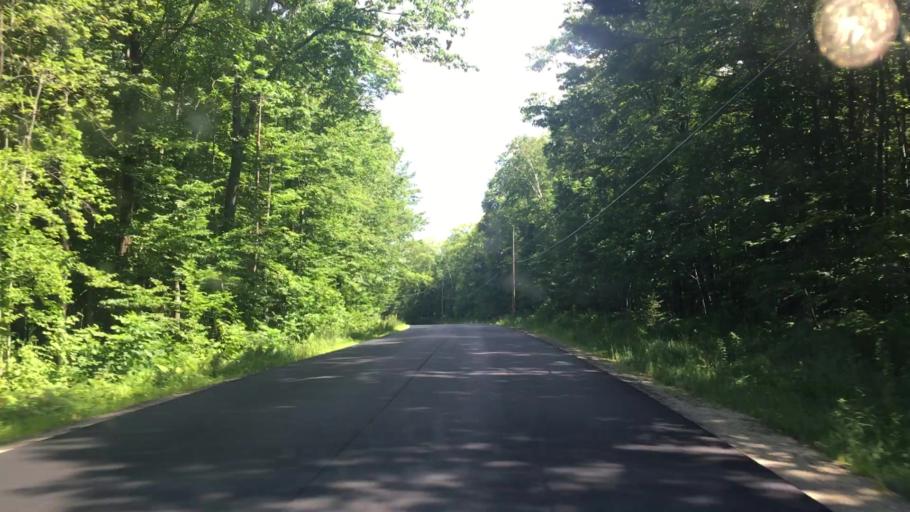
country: US
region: Maine
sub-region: Franklin County
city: Chesterville
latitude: 44.5708
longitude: -70.1498
